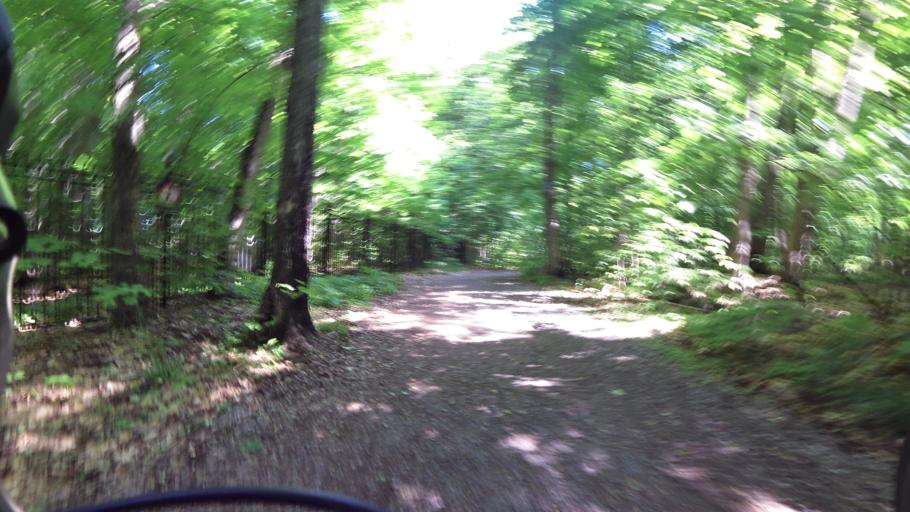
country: CA
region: Quebec
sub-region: Outaouais
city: Wakefield
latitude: 45.5292
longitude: -75.8651
